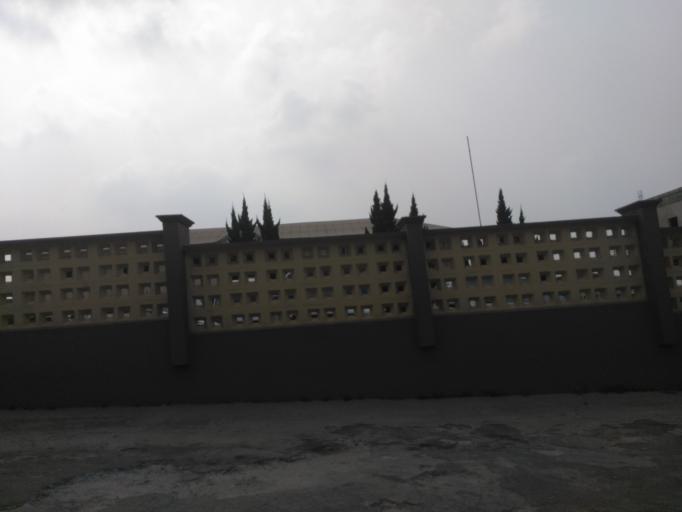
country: GH
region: Ashanti
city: Kumasi
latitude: 6.6922
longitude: -1.6155
